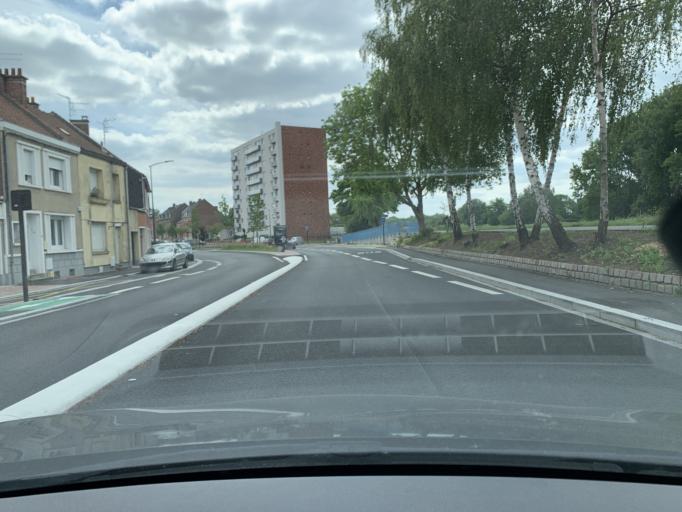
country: FR
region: Nord-Pas-de-Calais
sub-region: Departement du Nord
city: Douai
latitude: 50.3702
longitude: 3.0645
